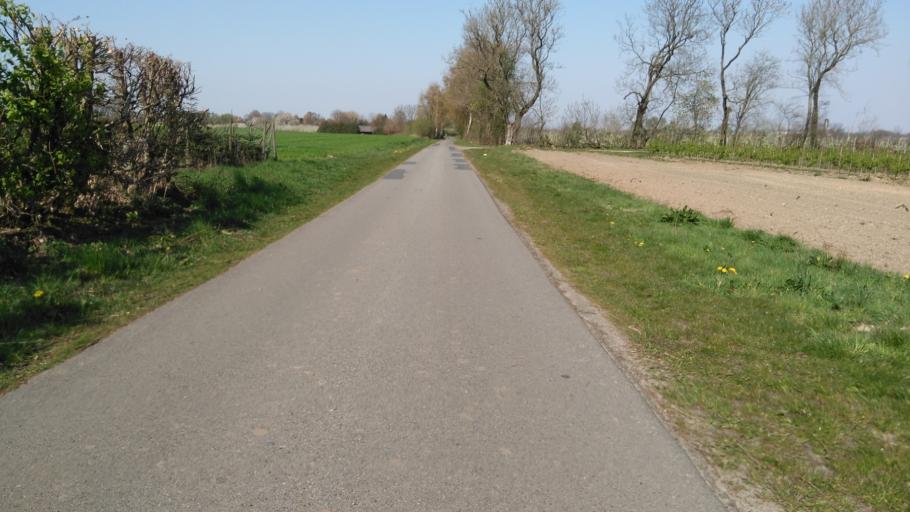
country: DE
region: Lower Saxony
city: Bliedersdorf
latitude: 53.4696
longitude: 9.5687
